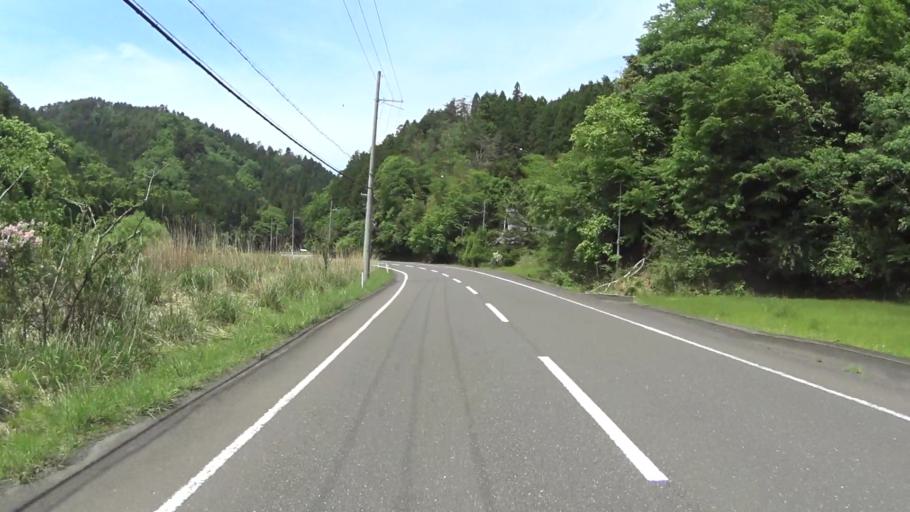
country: JP
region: Kyoto
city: Maizuru
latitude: 35.4023
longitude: 135.4637
